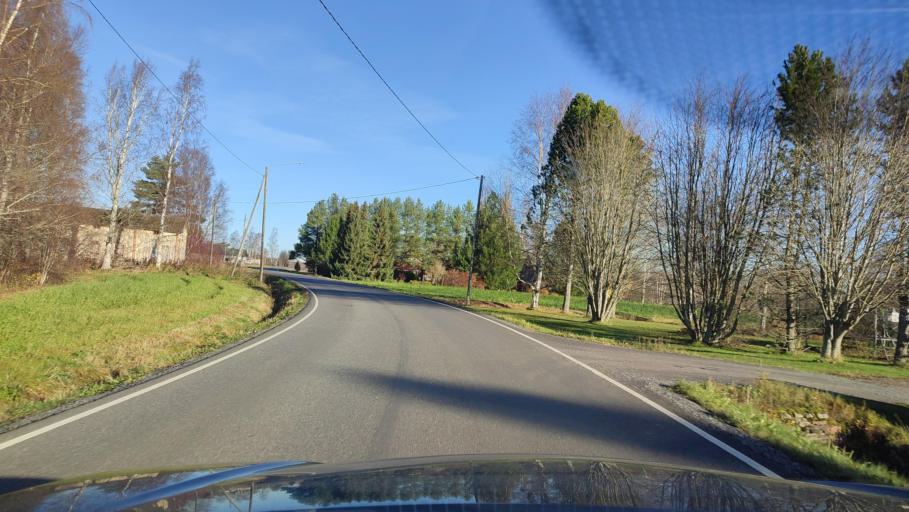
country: FI
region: Southern Ostrobothnia
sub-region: Suupohja
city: Karijoki
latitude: 62.2798
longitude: 21.7103
